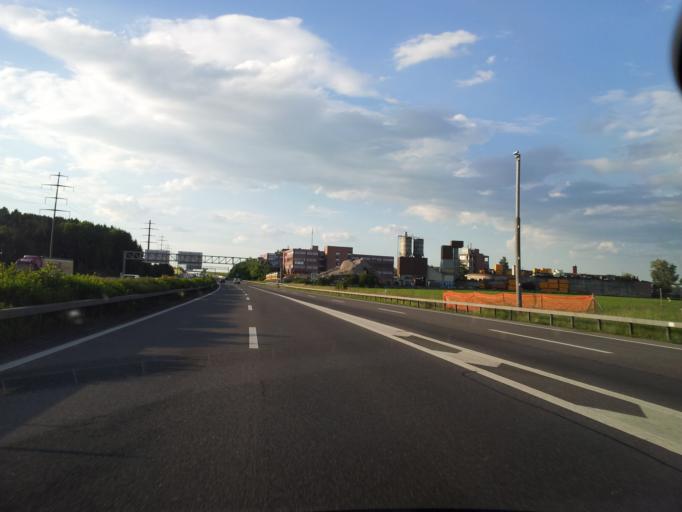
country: CH
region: Zug
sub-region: Zug
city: Hunenberg
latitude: 47.1582
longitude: 8.4332
